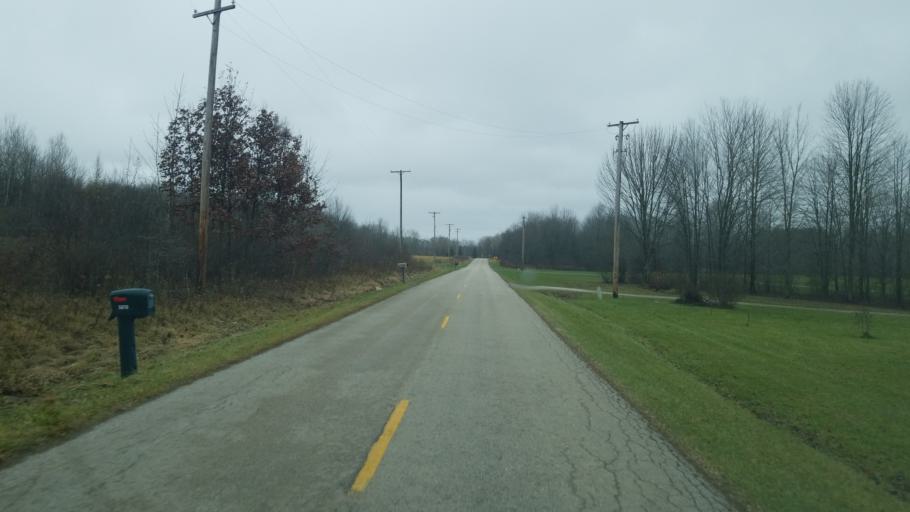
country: US
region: Ohio
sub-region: Ashtabula County
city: Roaming Shores
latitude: 41.5906
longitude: -80.7630
